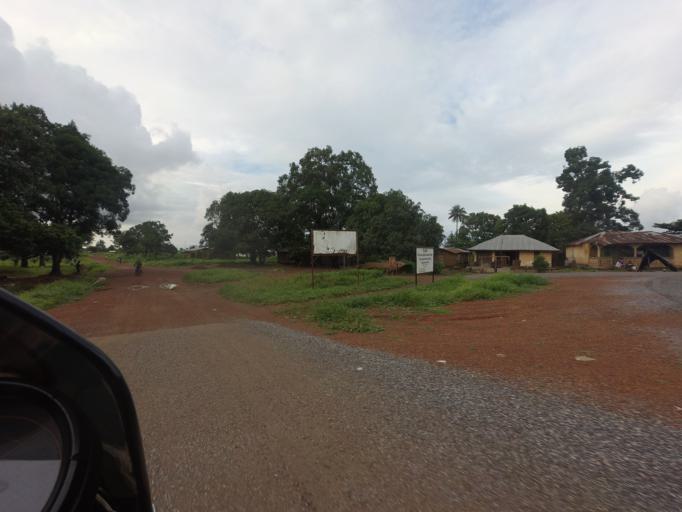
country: SL
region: Northern Province
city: Kambia
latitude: 9.0452
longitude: -12.9131
